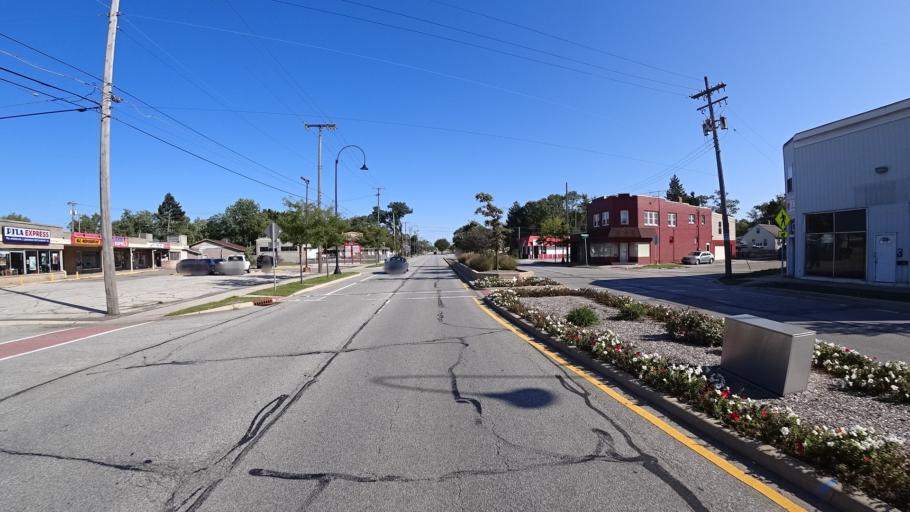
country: US
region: Indiana
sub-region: LaPorte County
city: Michigan City
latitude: 41.7111
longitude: -86.8788
